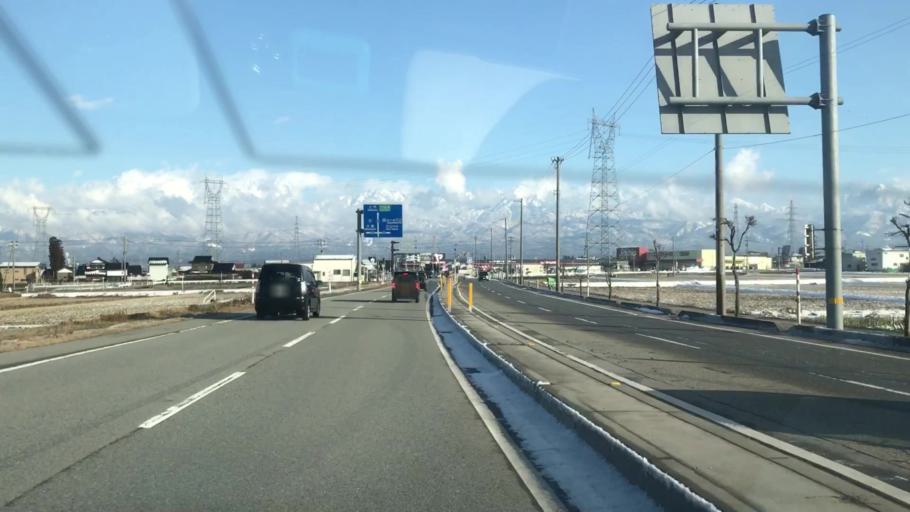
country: JP
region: Toyama
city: Toyama-shi
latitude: 36.6871
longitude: 137.2891
